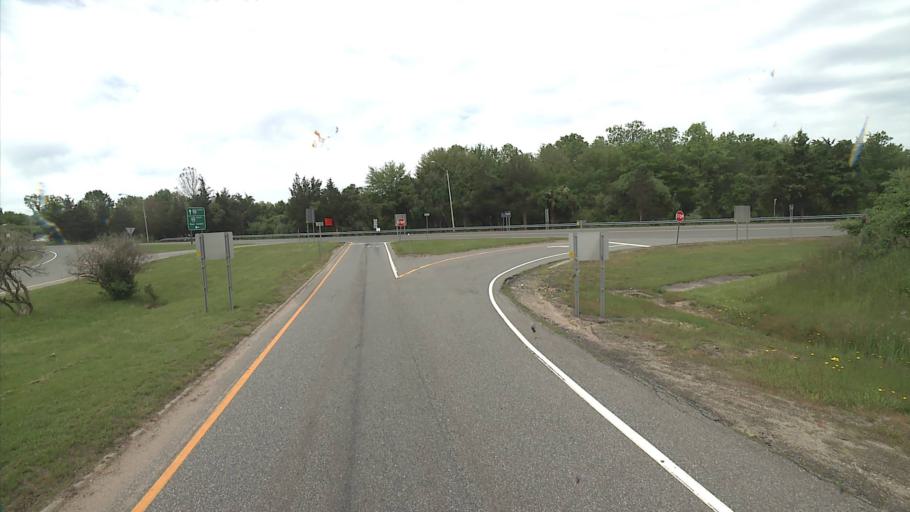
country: US
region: Connecticut
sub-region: New London County
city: Old Mystic
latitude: 41.3811
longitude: -71.9043
